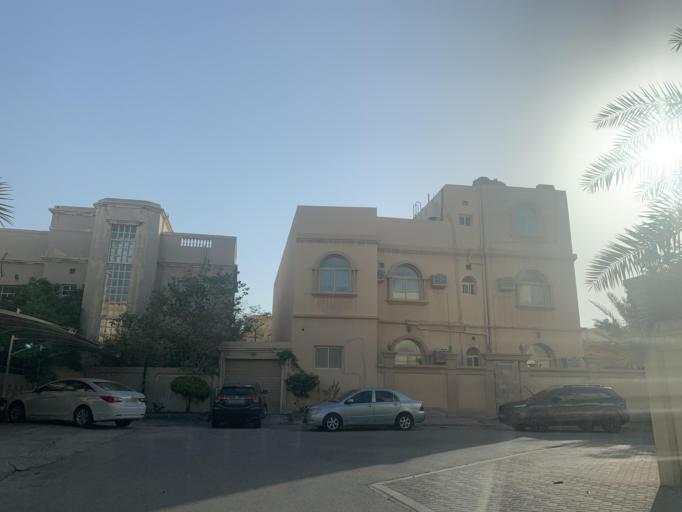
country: BH
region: Manama
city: Jidd Hafs
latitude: 26.2087
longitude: 50.5323
